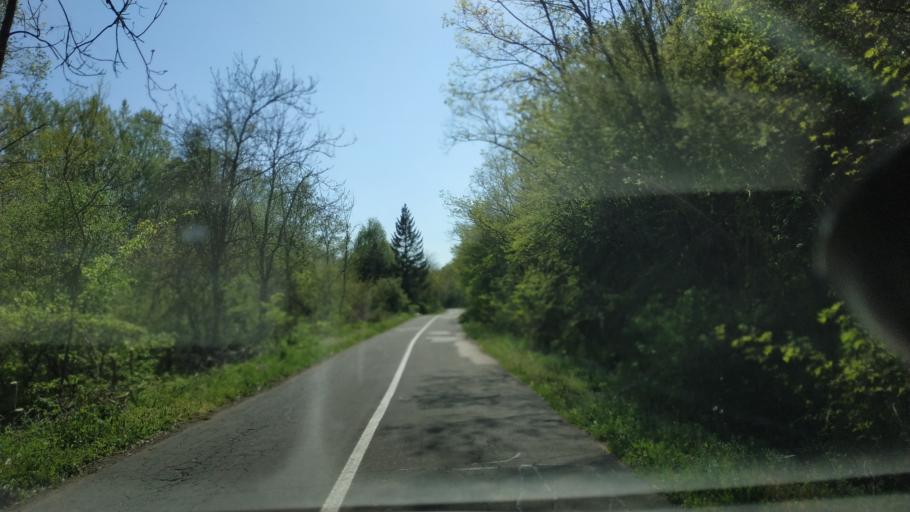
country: RS
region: Central Serbia
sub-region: Nisavski Okrug
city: Nis
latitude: 43.4179
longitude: 21.8414
